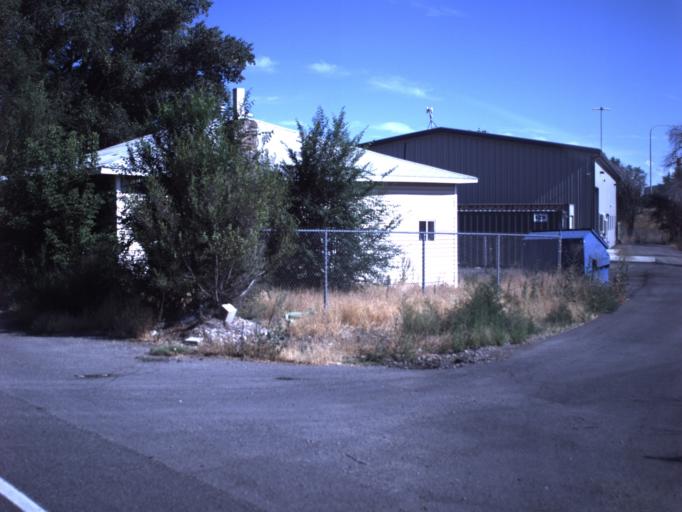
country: US
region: Utah
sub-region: Utah County
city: Lehi
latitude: 40.3916
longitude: -111.8340
